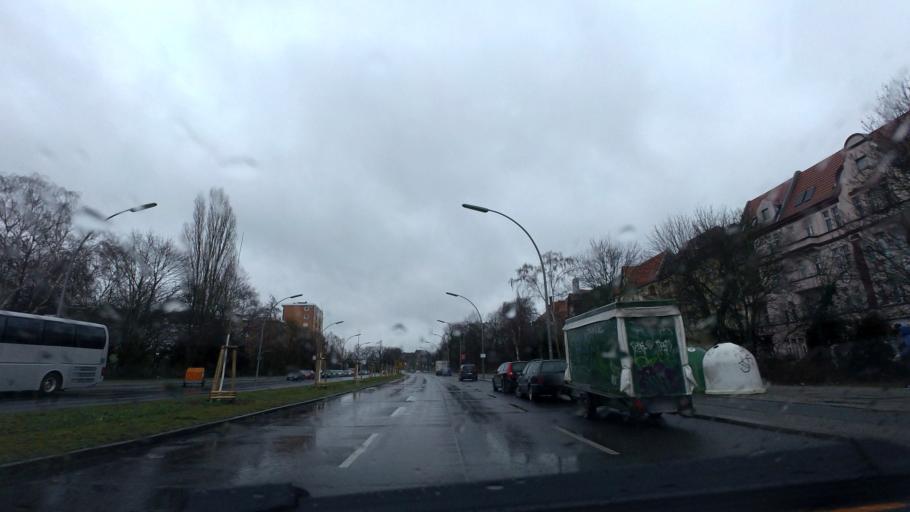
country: DE
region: Berlin
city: Spandau
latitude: 52.5422
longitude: 13.1995
